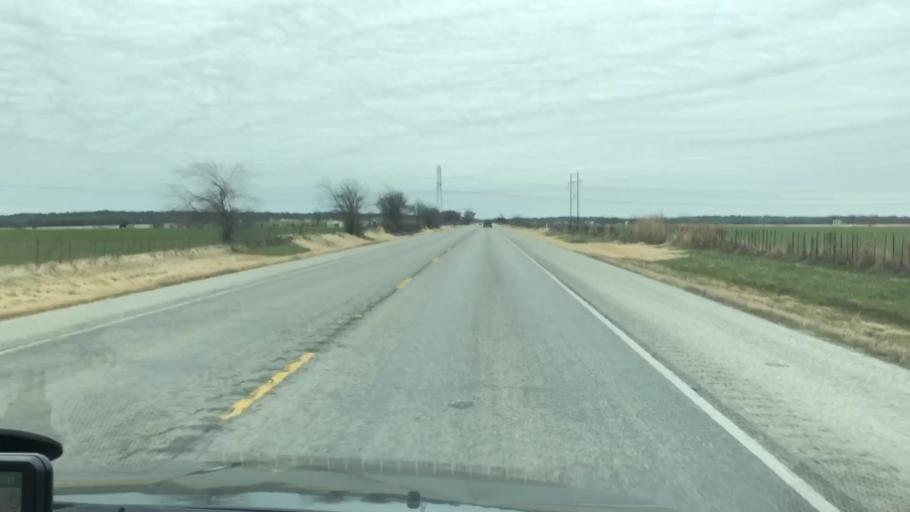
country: US
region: Texas
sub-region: Palo Pinto County
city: Mineral Wells
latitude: 32.9268
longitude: -98.0723
